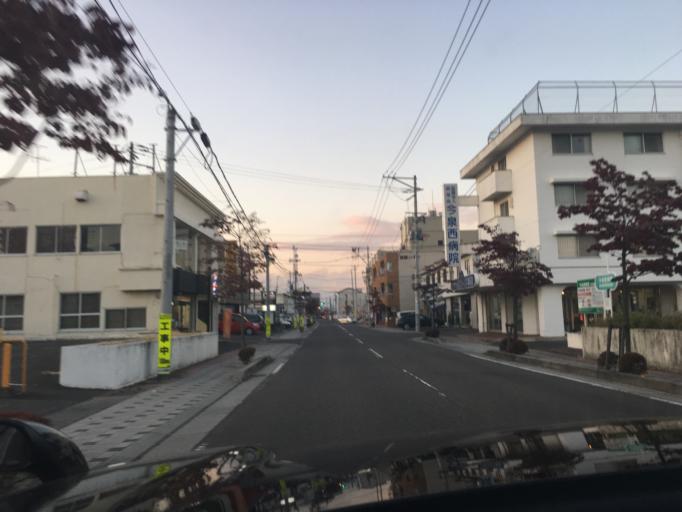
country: JP
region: Fukushima
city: Koriyama
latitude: 37.4039
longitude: 140.3578
